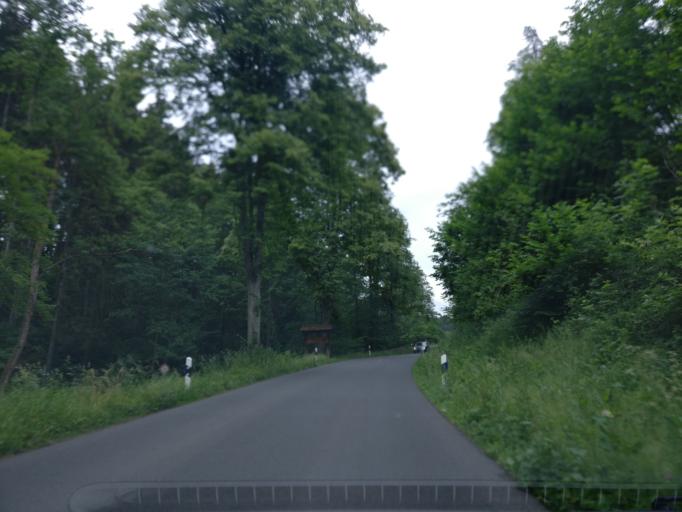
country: DE
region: Lower Saxony
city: Scheden
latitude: 51.4132
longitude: 9.7124
